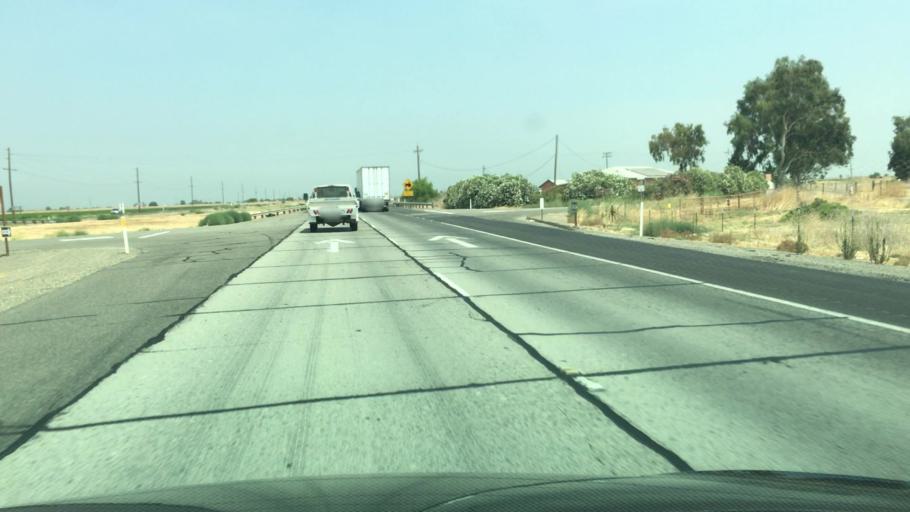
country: US
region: California
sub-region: Merced County
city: Los Banos
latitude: 37.0556
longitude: -120.7881
